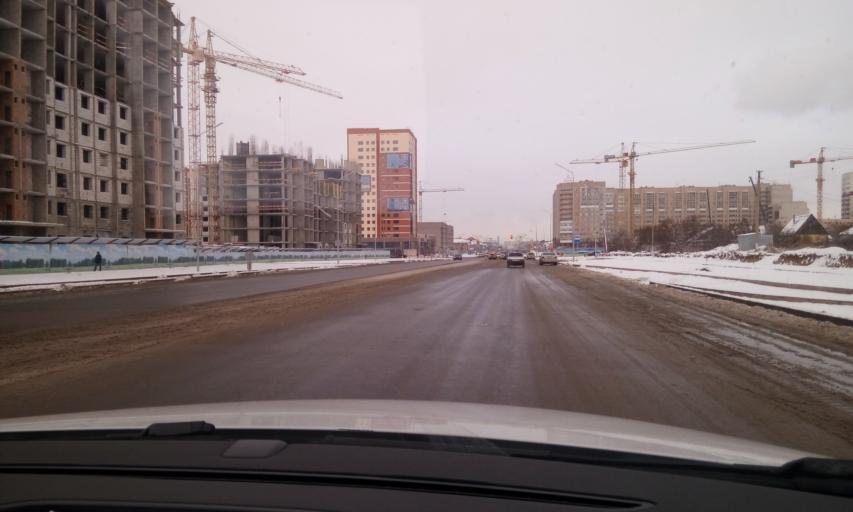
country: KZ
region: Astana Qalasy
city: Astana
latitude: 51.1270
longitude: 71.4988
